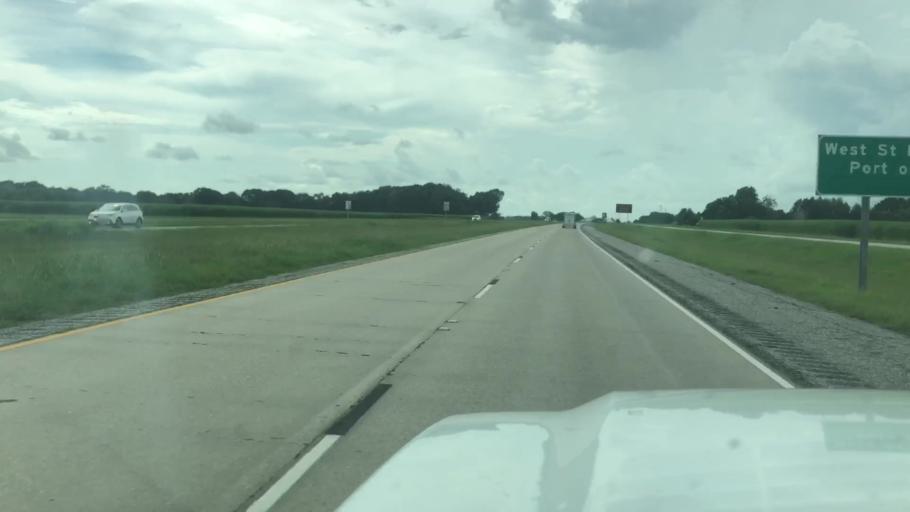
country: US
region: Louisiana
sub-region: Iberia Parish
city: Jeanerette
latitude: 29.8610
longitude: -91.6216
